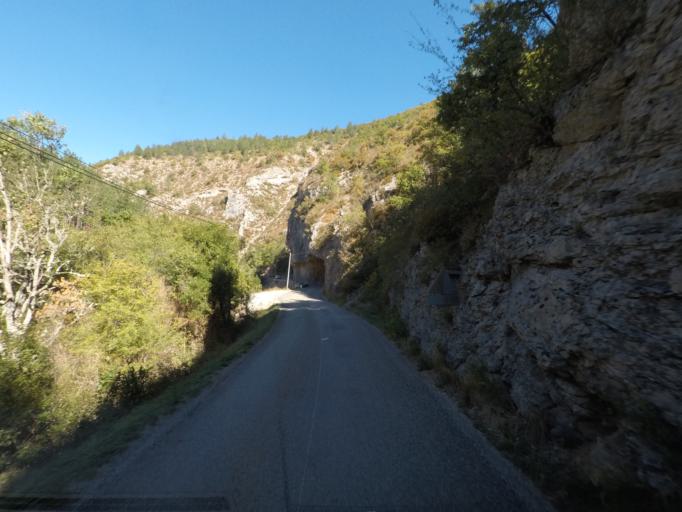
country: FR
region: Rhone-Alpes
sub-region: Departement de la Drome
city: Die
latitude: 44.6333
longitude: 5.2962
